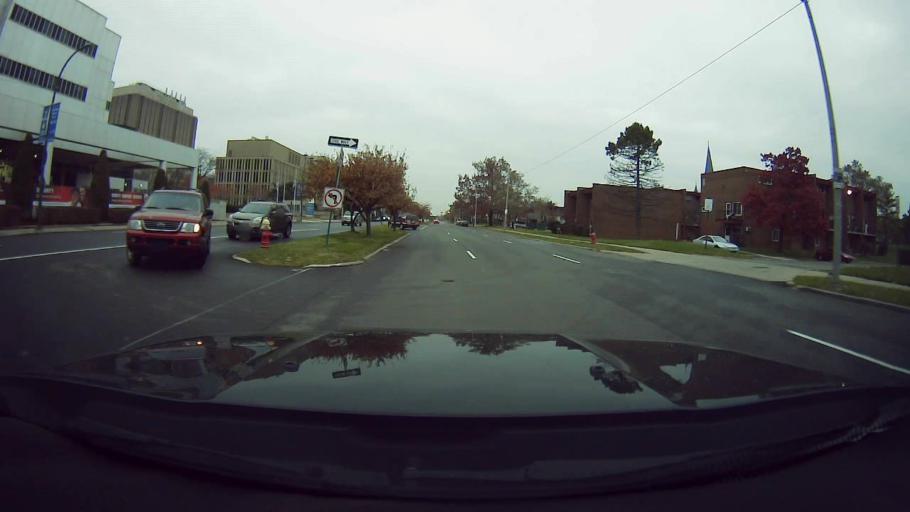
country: US
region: Michigan
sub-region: Wayne County
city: Detroit
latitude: 42.3539
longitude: -83.0531
